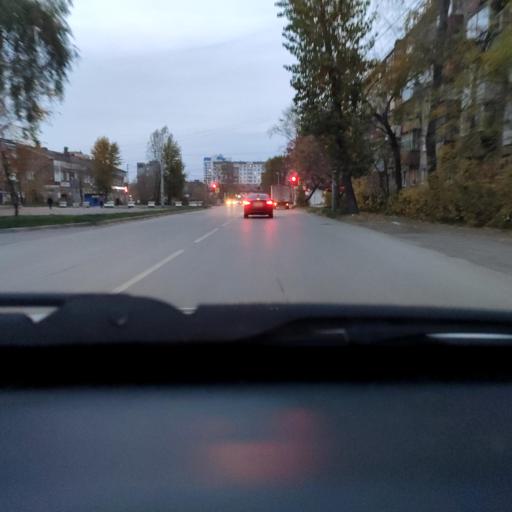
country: RU
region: Perm
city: Perm
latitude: 57.9722
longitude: 56.2098
